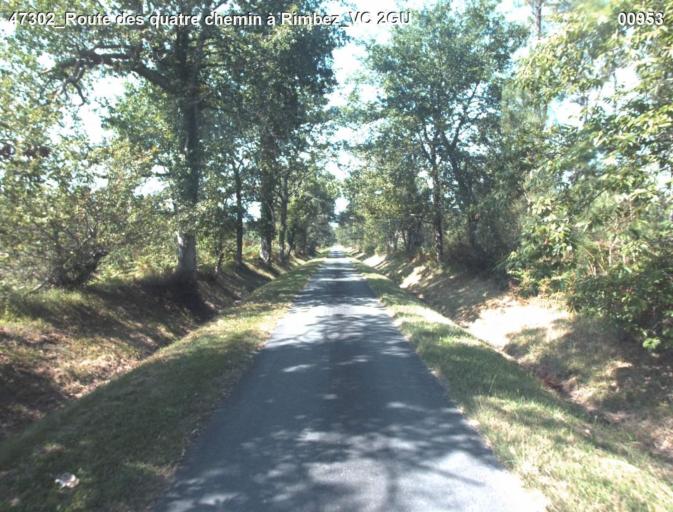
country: FR
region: Aquitaine
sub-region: Departement des Landes
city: Gabarret
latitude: 44.0300
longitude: 0.0817
